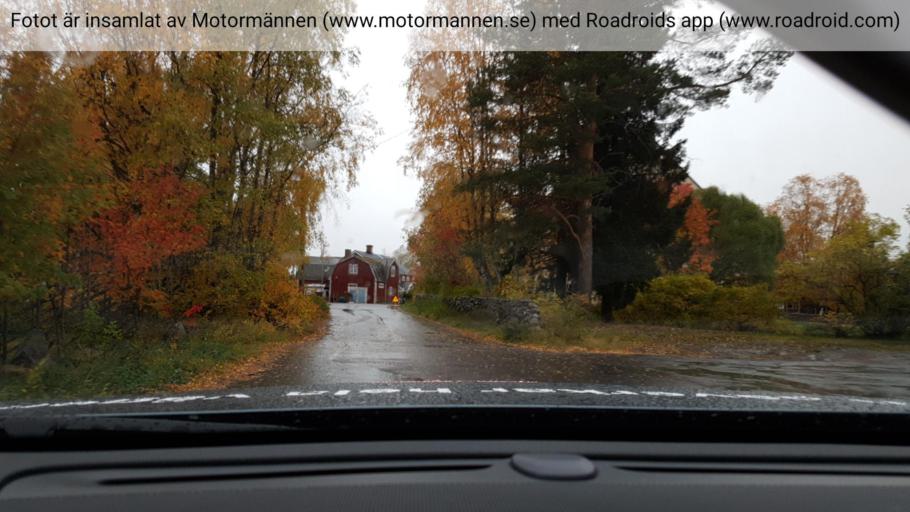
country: SE
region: Norrbotten
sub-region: Lulea Kommun
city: Sodra Sunderbyn
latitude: 65.6582
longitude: 21.9430
